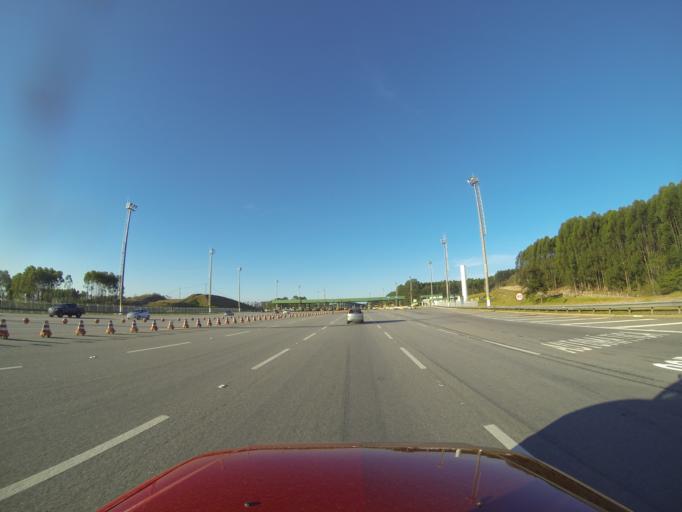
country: BR
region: Sao Paulo
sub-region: Jacarei
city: Jacarei
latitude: -23.2848
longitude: -45.8622
